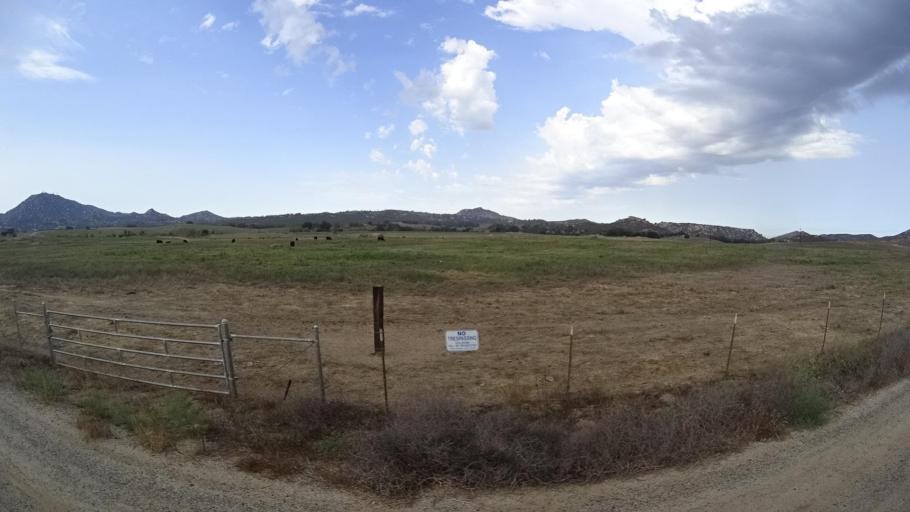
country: US
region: California
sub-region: San Diego County
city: San Pasqual
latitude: 33.0494
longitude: -116.9362
